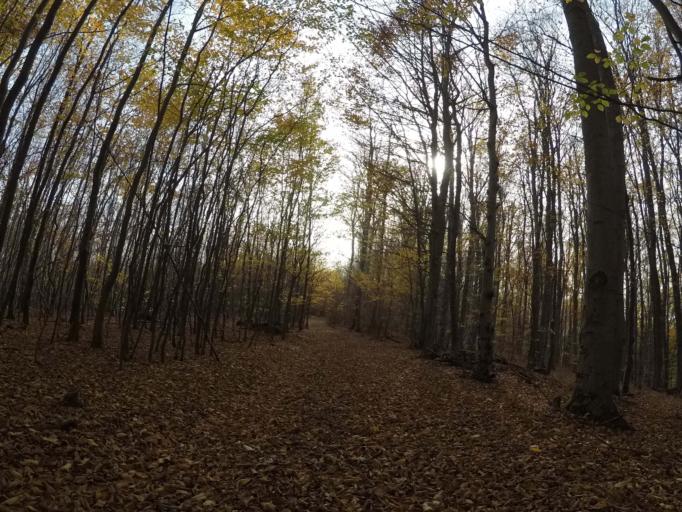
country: SK
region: Presovsky
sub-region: Okres Presov
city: Presov
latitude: 48.9542
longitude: 21.1859
